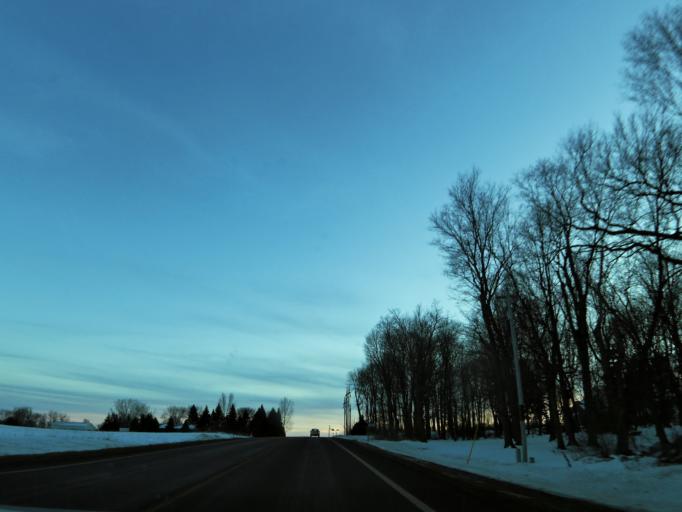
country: US
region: Minnesota
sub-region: Carver County
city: Chaska
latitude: 44.7558
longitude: -93.5614
